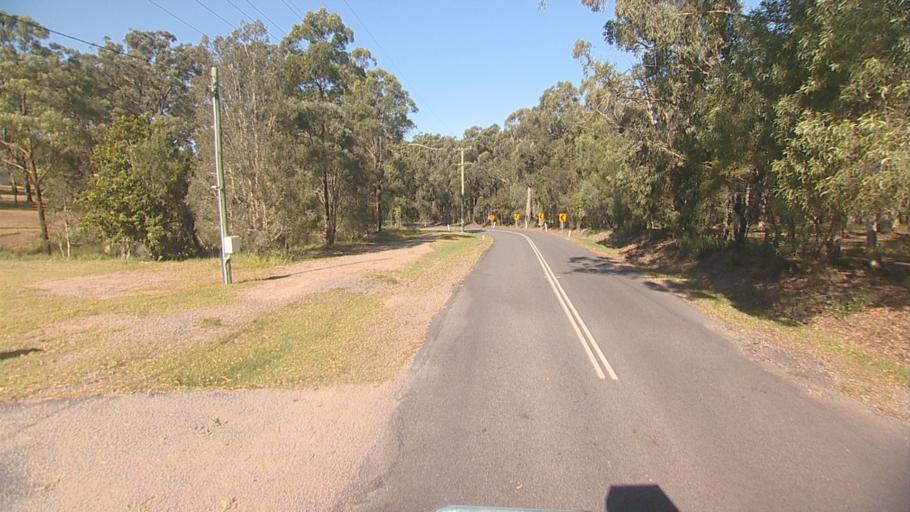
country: AU
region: Queensland
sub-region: Logan
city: Springwood
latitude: -27.5971
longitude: 153.1615
